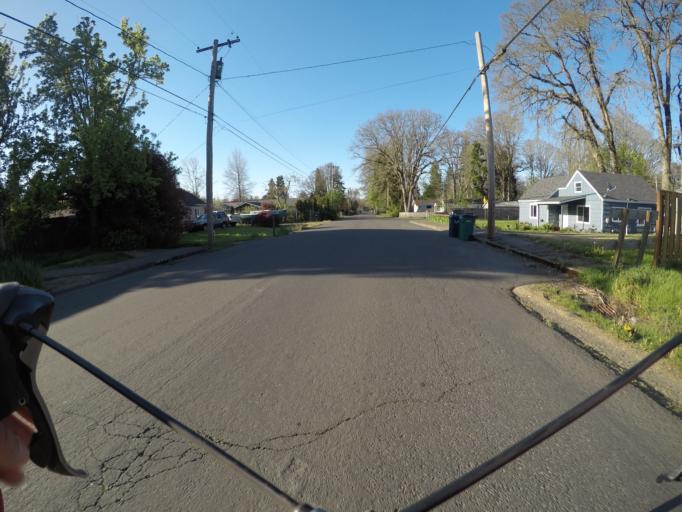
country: US
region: Oregon
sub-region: Washington County
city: Aloha
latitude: 45.4969
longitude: -122.8642
